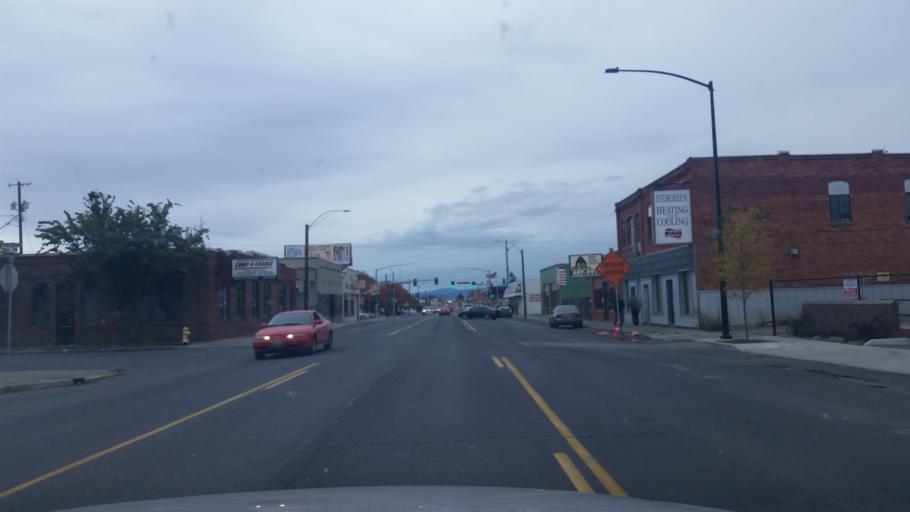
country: US
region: Washington
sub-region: Spokane County
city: Spokane
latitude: 47.6572
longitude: -117.3892
